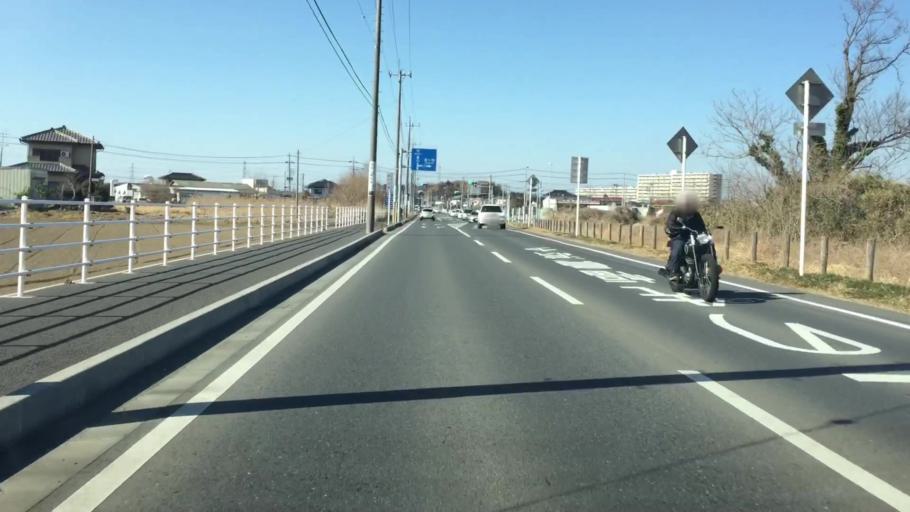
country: JP
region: Ibaraki
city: Ryugasaki
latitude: 35.8429
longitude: 140.1345
